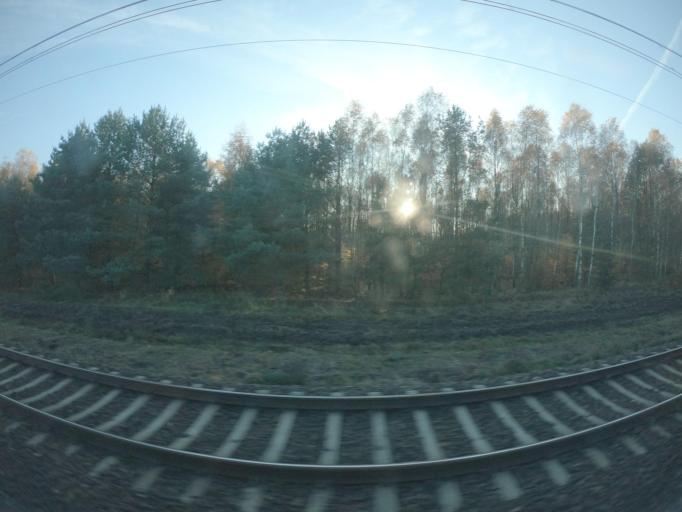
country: PL
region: Lubusz
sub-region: Powiat slubicki
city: Rzepin
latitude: 52.2717
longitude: 14.9232
